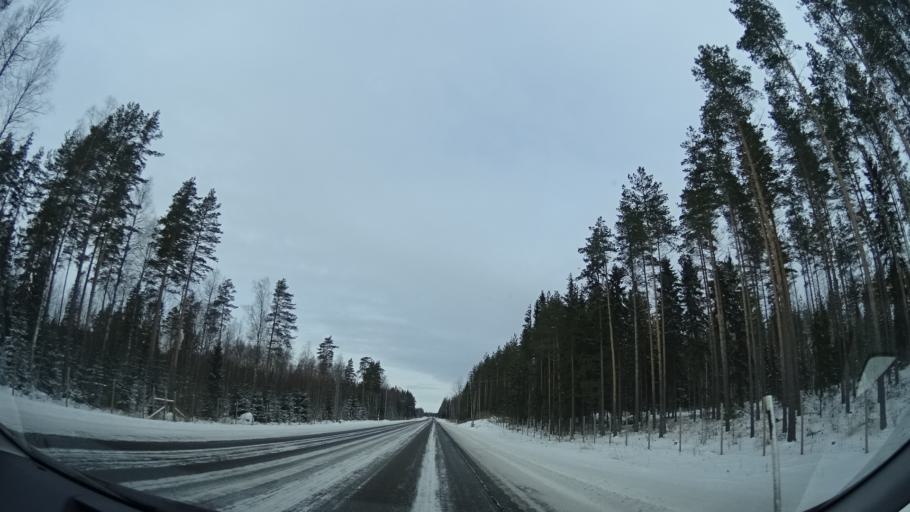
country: FI
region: Uusimaa
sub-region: Helsinki
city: Kaerkoelae
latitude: 60.6642
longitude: 23.8389
